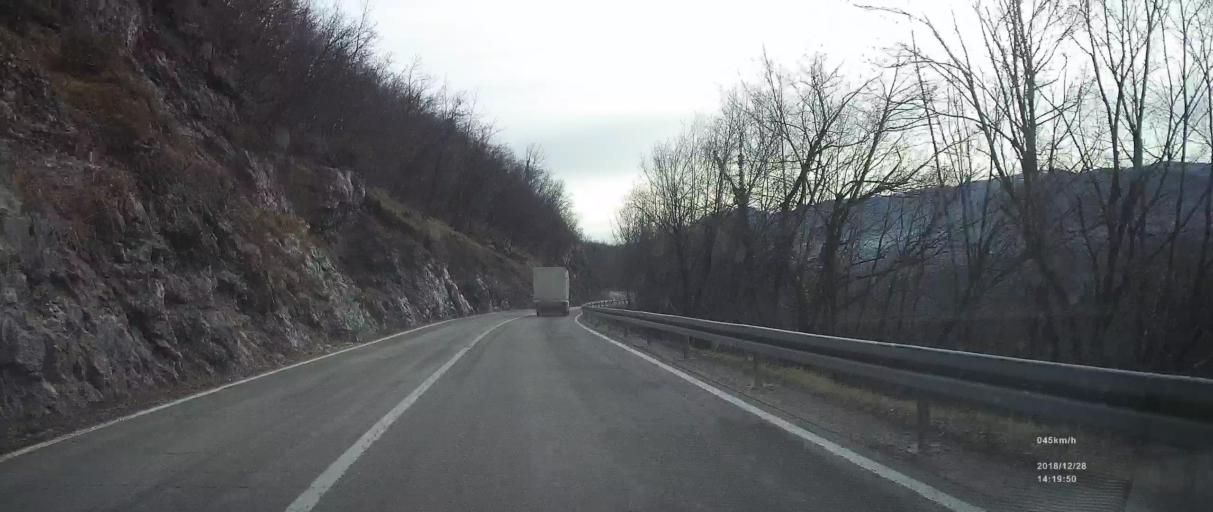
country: HR
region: Primorsko-Goranska
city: Vrbovsko
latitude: 45.4025
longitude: 15.0715
